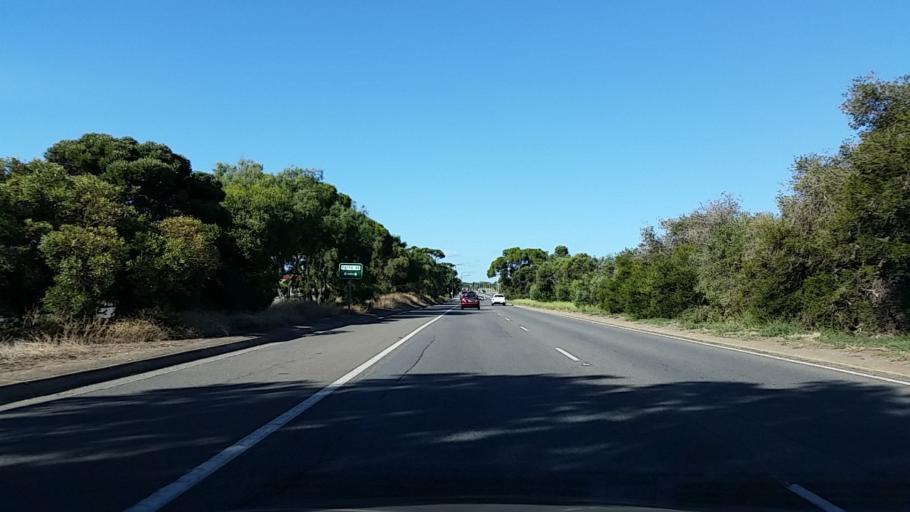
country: AU
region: South Australia
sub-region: Marion
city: Happy Valley
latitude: -35.0815
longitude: 138.5135
